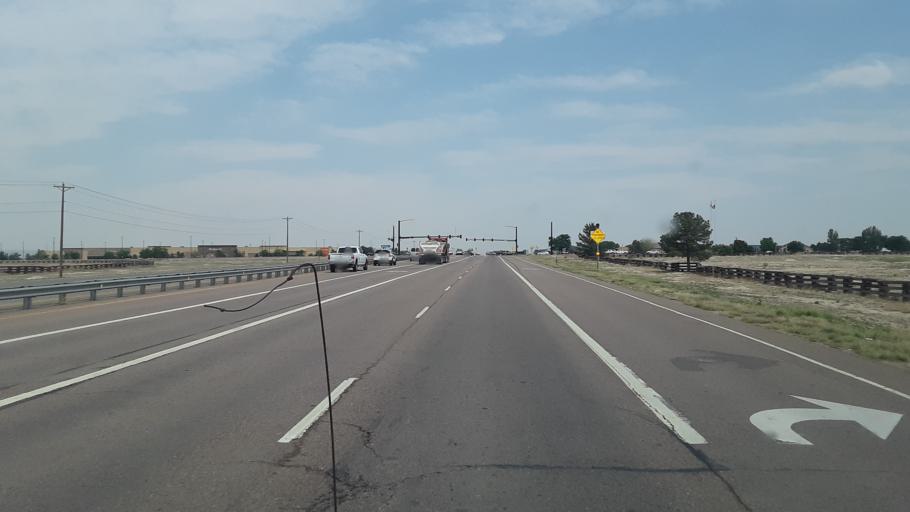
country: US
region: Colorado
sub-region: Pueblo County
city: Pueblo West
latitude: 38.3363
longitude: -104.7472
